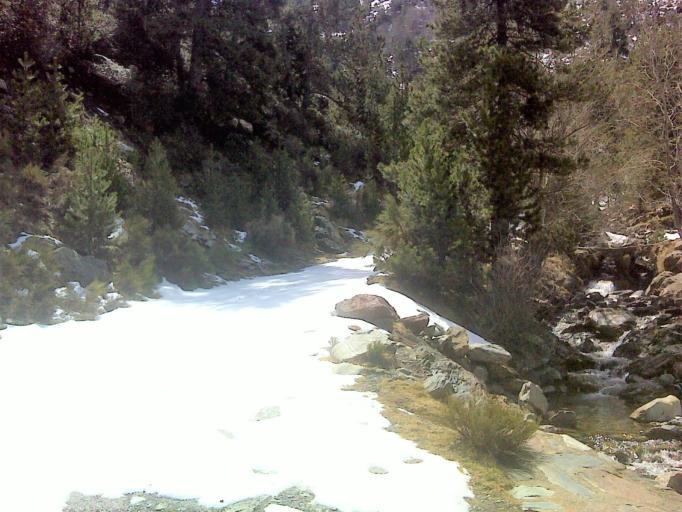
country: ES
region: Catalonia
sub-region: Provincia de Girona
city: Planoles
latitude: 42.4170
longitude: 2.1040
